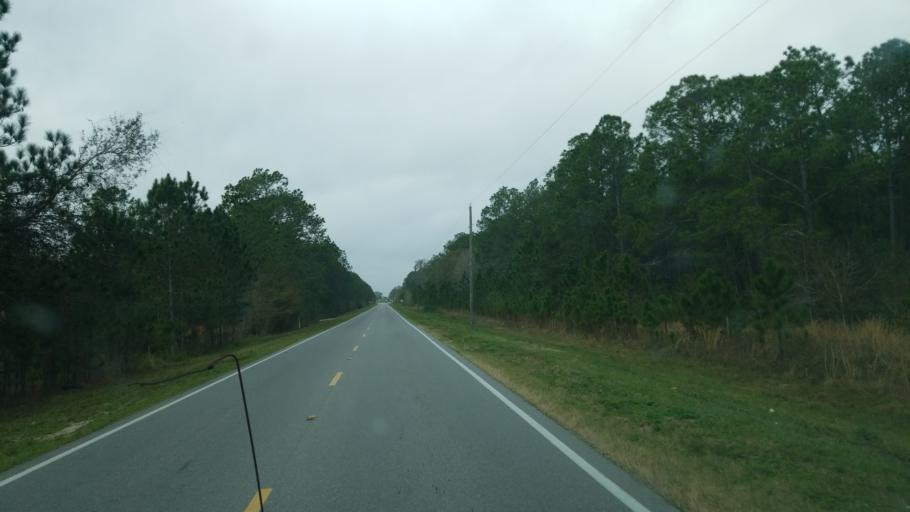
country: US
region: Florida
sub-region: Polk County
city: Polk City
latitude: 28.2586
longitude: -81.8160
